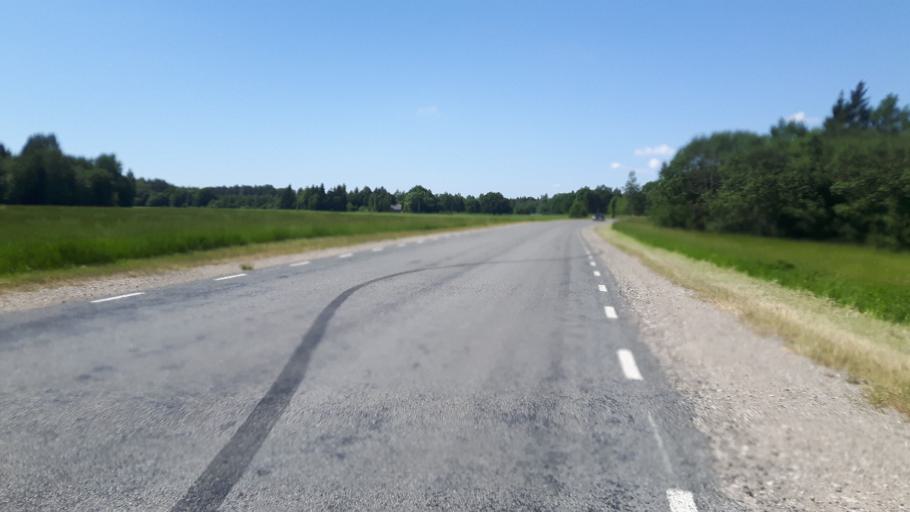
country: EE
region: Paernumaa
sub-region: Tootsi vald
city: Tootsi
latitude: 58.4974
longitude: 24.8772
